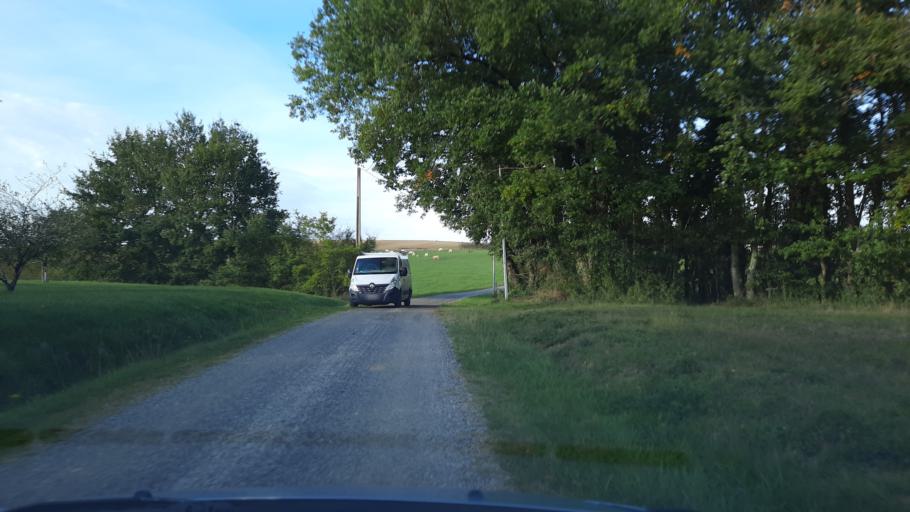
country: FR
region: Midi-Pyrenees
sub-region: Departement du Tarn-et-Garonne
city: Molieres
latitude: 44.1832
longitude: 1.3123
